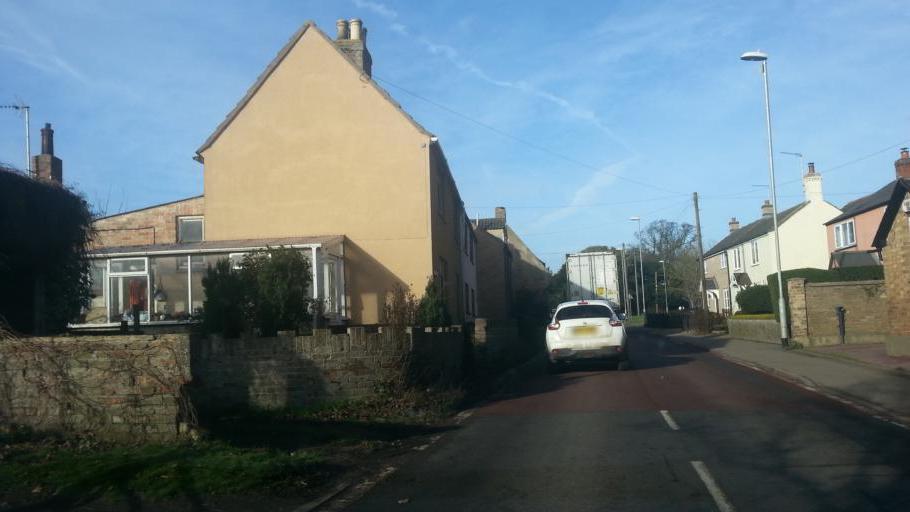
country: GB
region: England
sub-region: Cambridgeshire
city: Ramsey
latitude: 52.4377
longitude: -0.1114
